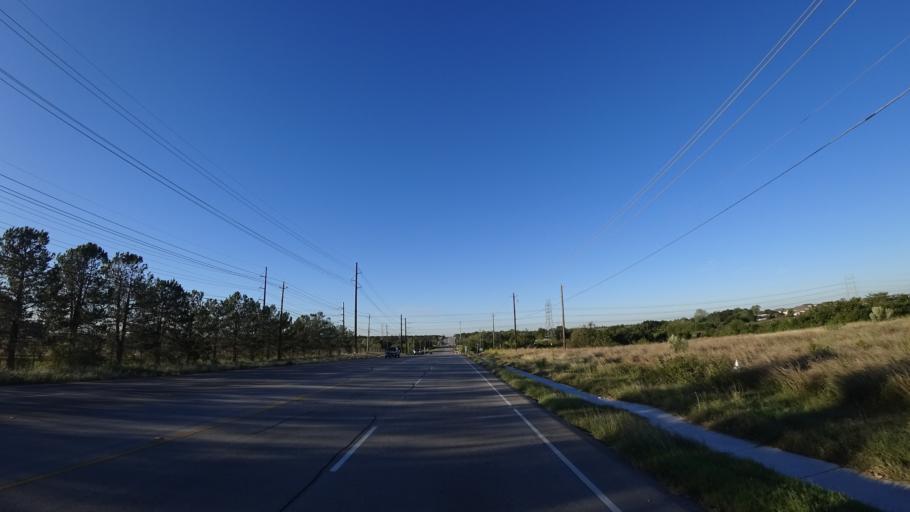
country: US
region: Texas
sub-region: Travis County
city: Manor
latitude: 30.3092
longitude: -97.6165
